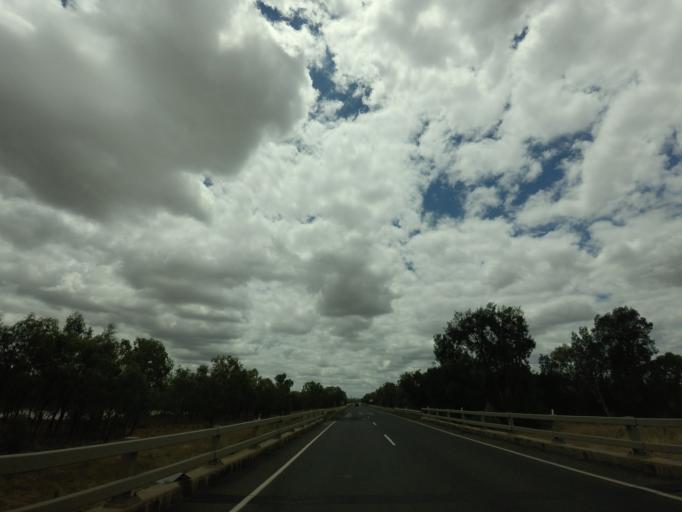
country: AU
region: Queensland
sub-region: Goondiwindi
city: Goondiwindi
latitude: -28.3990
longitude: 150.3104
